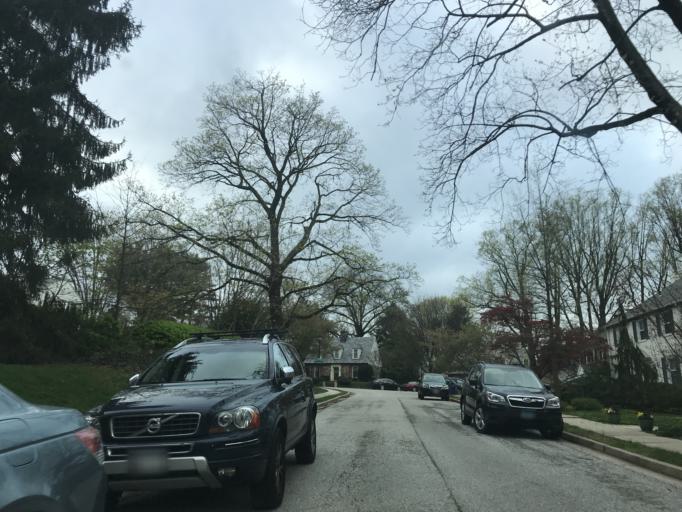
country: US
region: Maryland
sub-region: Baltimore County
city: Towson
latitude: 39.3891
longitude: -76.6013
